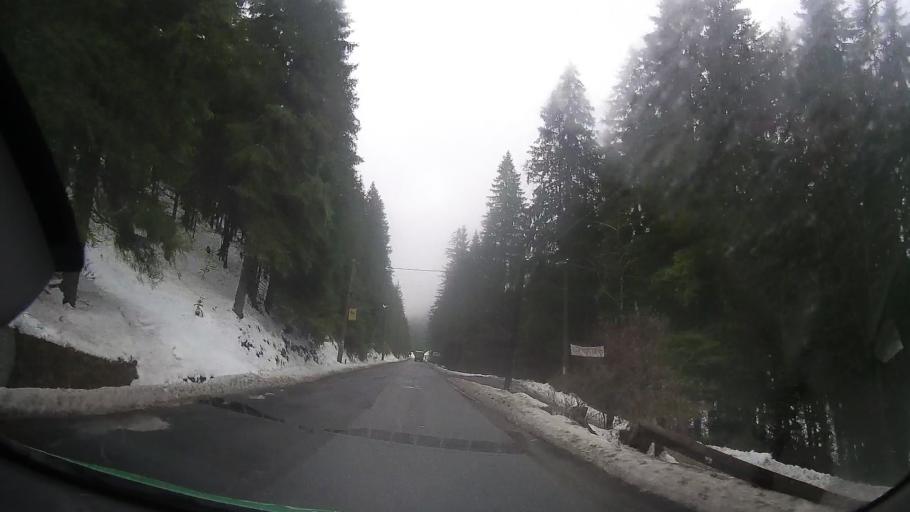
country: RO
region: Neamt
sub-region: Comuna Bicaz Chei
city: Bicaz Chei
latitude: 46.7826
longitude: 25.7860
